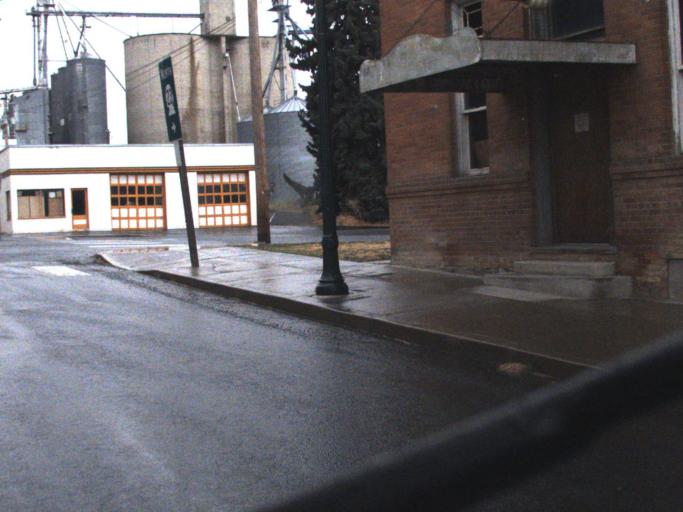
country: US
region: Washington
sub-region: Lincoln County
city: Davenport
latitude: 47.4791
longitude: -118.2547
